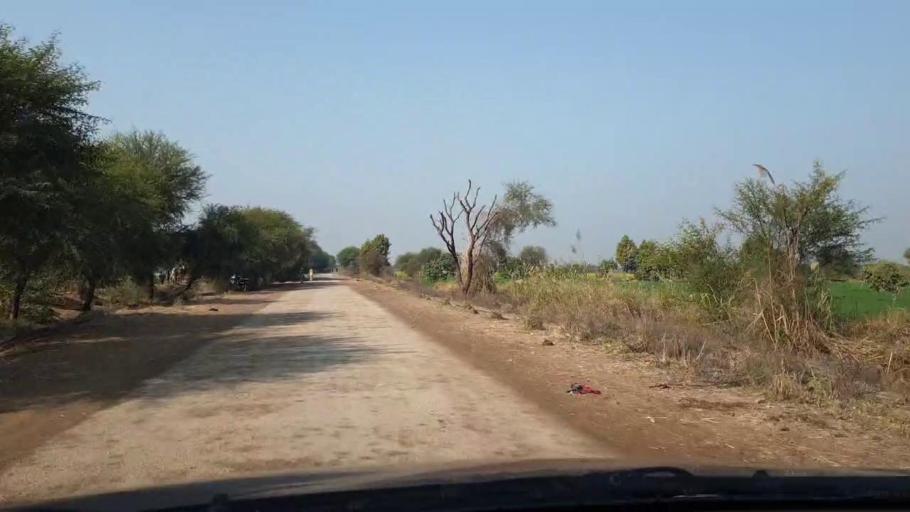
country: PK
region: Sindh
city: Jhol
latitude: 25.9614
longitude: 68.9673
